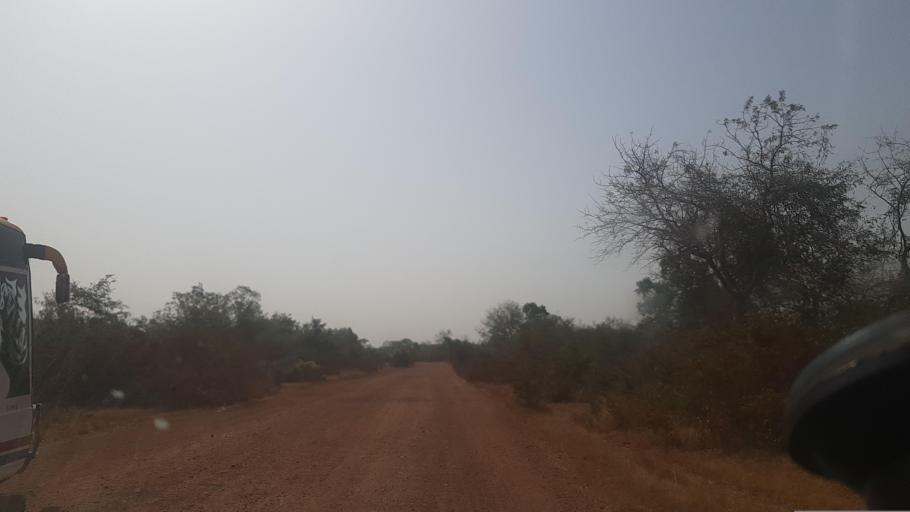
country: ML
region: Segou
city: Baroueli
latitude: 13.0714
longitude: -6.4802
